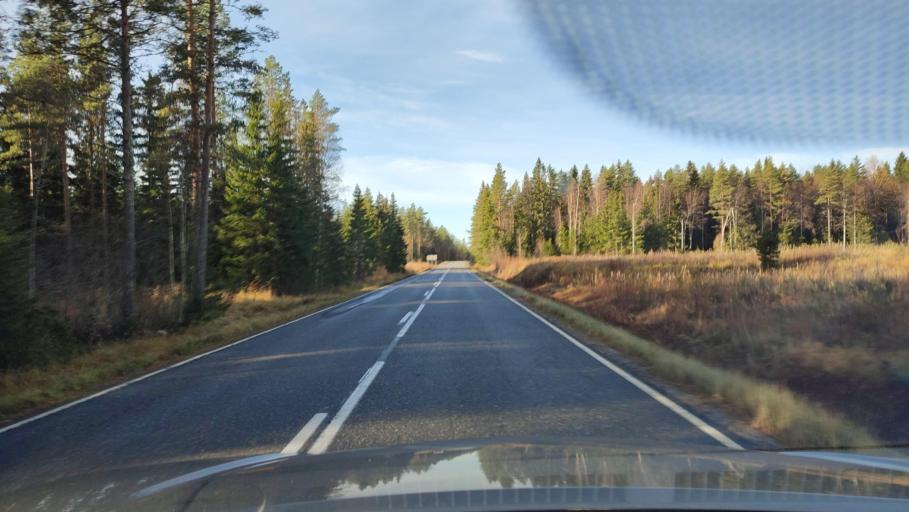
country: FI
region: Southern Ostrobothnia
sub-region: Suupohja
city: Teuva
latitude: 62.4594
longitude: 21.5583
